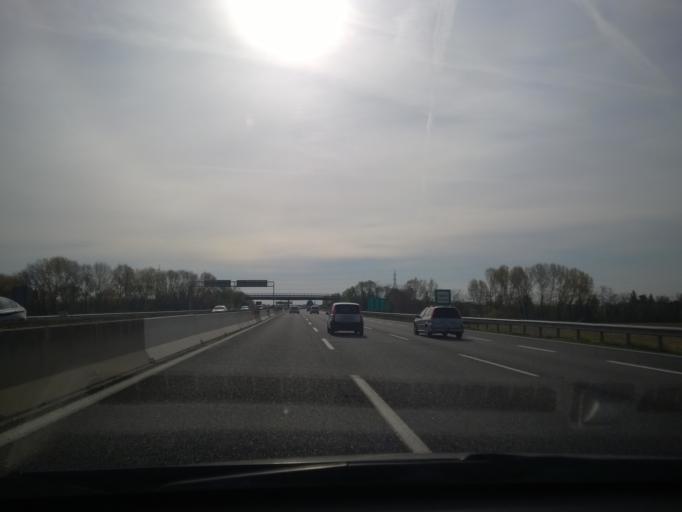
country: IT
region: Emilia-Romagna
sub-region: Forli-Cesena
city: Forli
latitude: 44.2504
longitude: 12.0966
